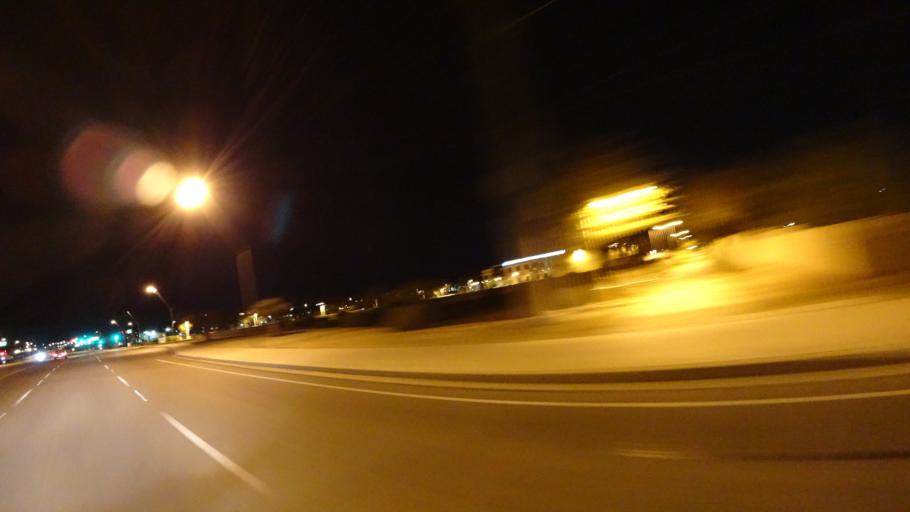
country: US
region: Arizona
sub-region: Maricopa County
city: Tempe Junction
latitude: 33.4279
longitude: -111.9609
